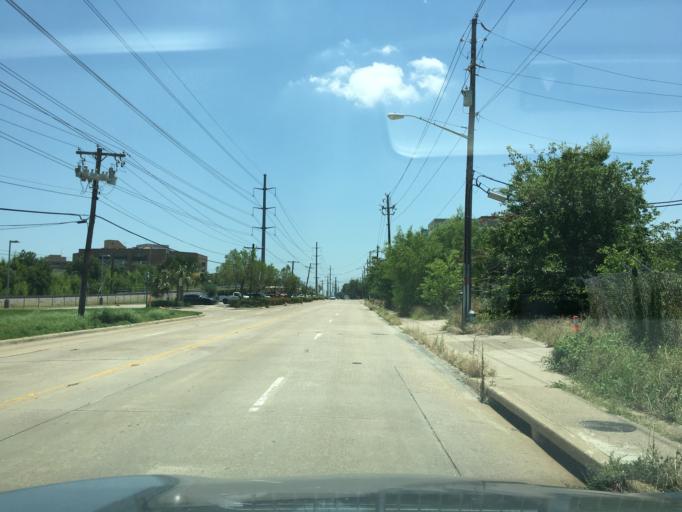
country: US
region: Texas
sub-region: Dallas County
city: University Park
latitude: 32.8865
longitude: -96.7653
